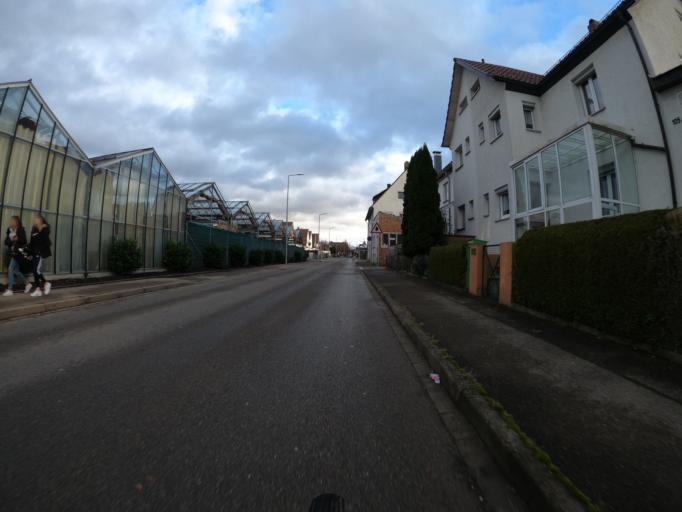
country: DE
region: Baden-Wuerttemberg
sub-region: Regierungsbezirk Stuttgart
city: Eislingen
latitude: 48.6952
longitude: 9.6946
